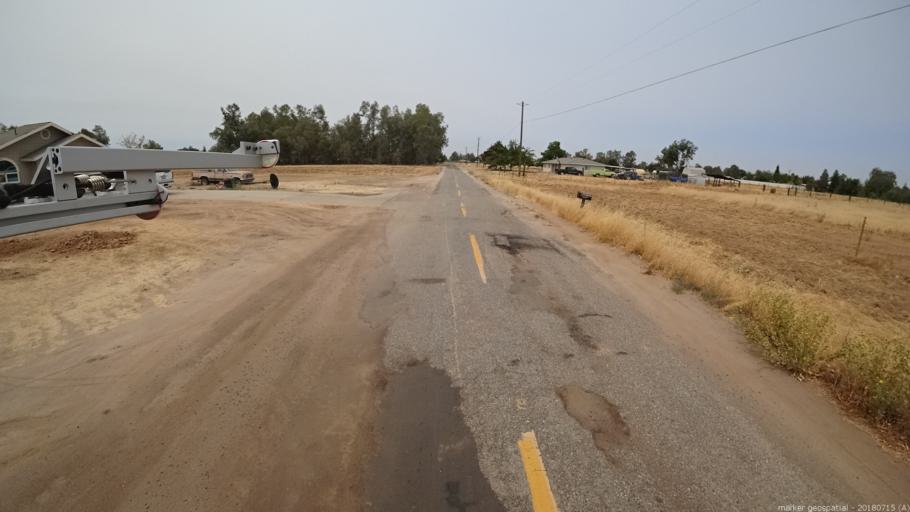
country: US
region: California
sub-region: Madera County
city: Madera Acres
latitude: 37.0067
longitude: -120.0956
